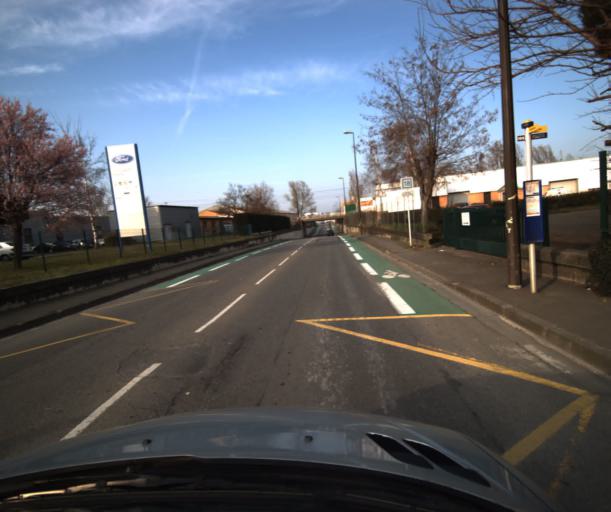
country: FR
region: Midi-Pyrenees
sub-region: Departement de la Haute-Garonne
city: Ramonville-Saint-Agne
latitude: 43.5669
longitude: 1.4898
